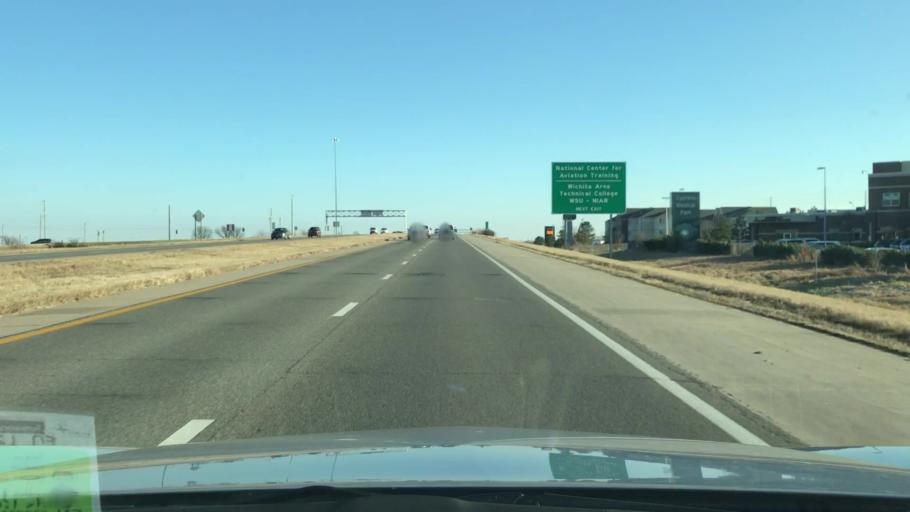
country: US
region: Kansas
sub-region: Sedgwick County
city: Bellaire
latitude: 37.7403
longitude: -97.2297
